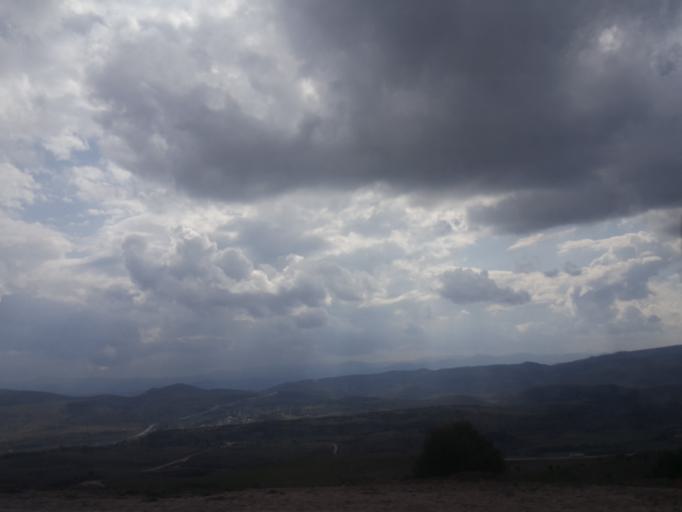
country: TR
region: Tokat
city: Bereketli
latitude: 40.5503
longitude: 37.3068
